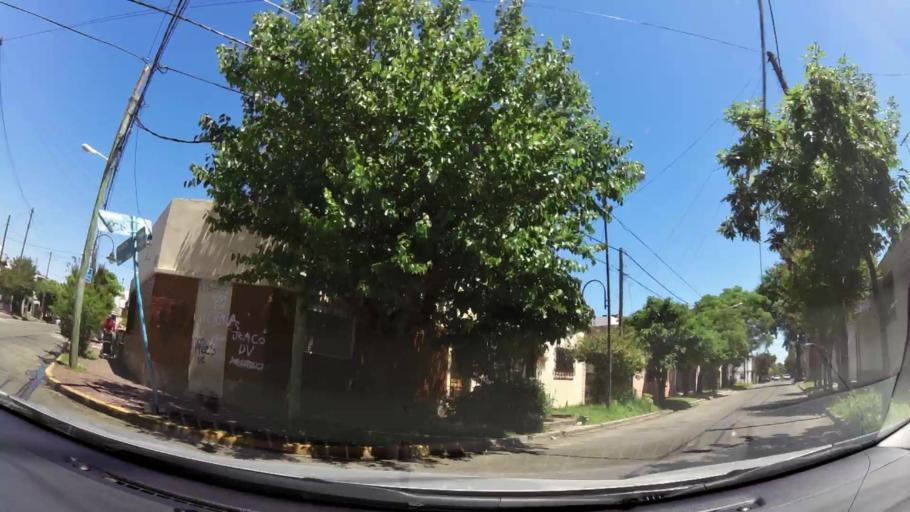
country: AR
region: Buenos Aires
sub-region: Partido de San Isidro
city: San Isidro
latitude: -34.4560
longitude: -58.5480
